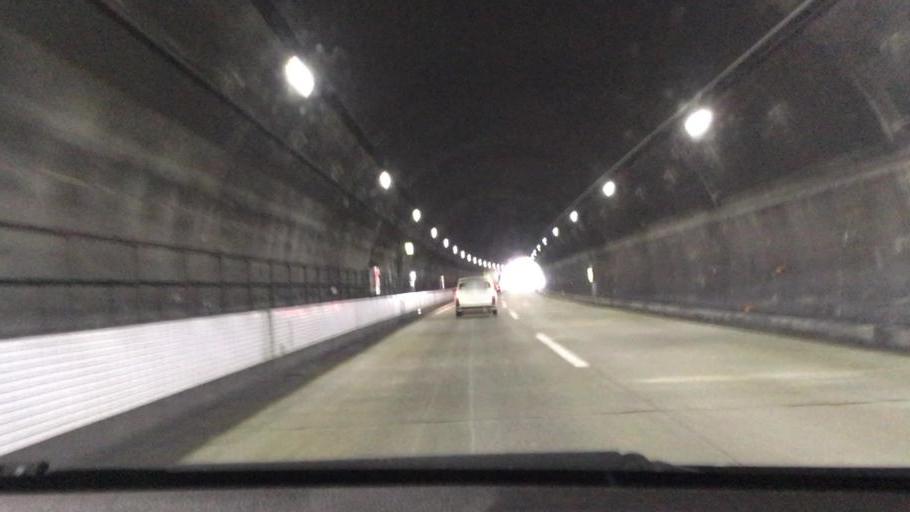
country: JP
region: Yamaguchi
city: Tokuyama
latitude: 34.0694
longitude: 131.7072
